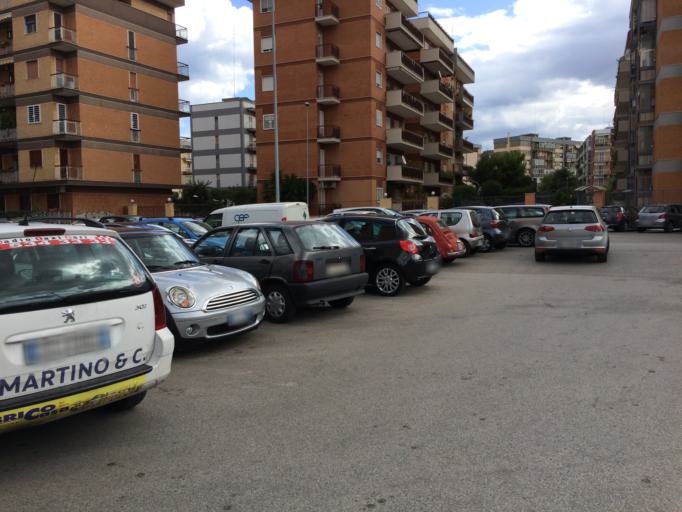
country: IT
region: Apulia
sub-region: Provincia di Bari
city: Bari
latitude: 41.0996
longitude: 16.8573
